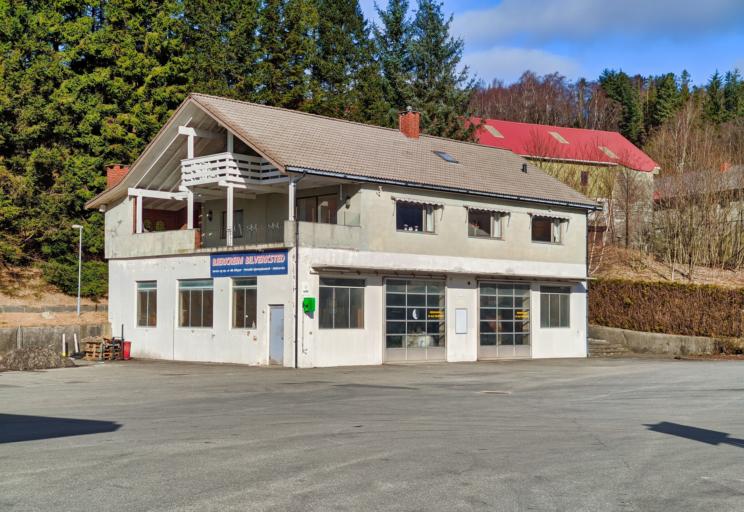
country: NO
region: Rogaland
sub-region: Bjerkreim
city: Vikesa
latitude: 58.6325
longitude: 6.0779
